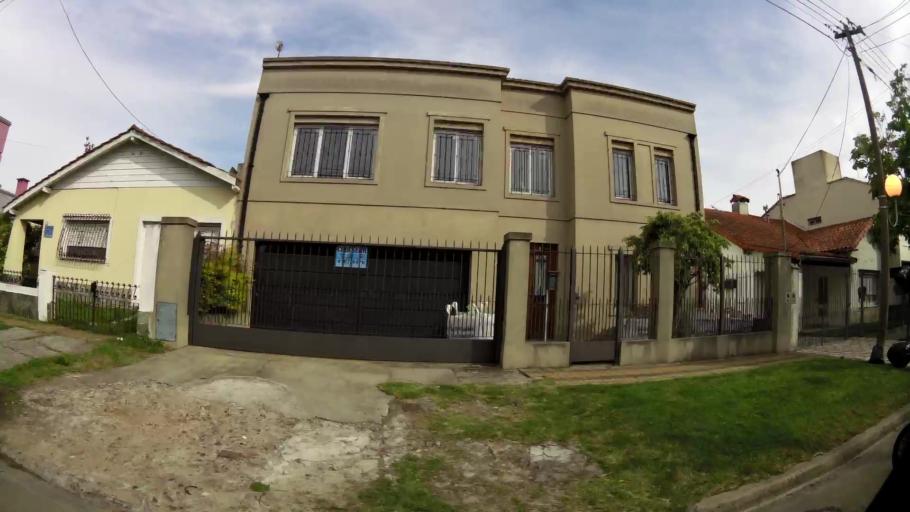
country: AR
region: Buenos Aires
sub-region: Partido de Quilmes
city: Quilmes
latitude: -34.7535
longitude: -58.2786
